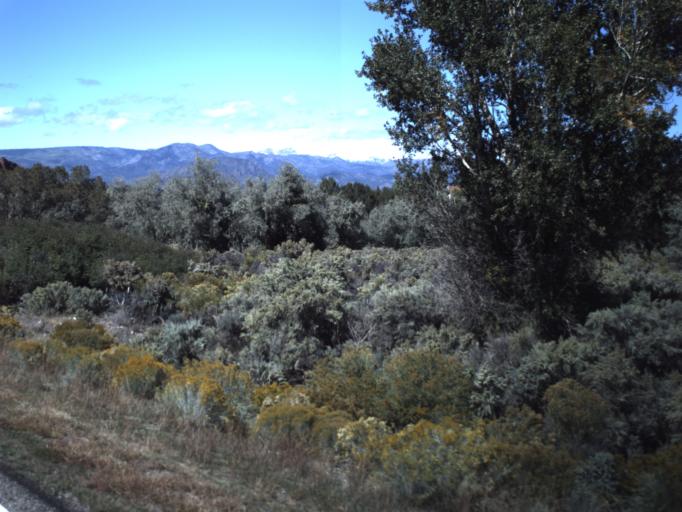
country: US
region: Utah
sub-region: Piute County
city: Junction
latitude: 38.2018
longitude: -112.1743
